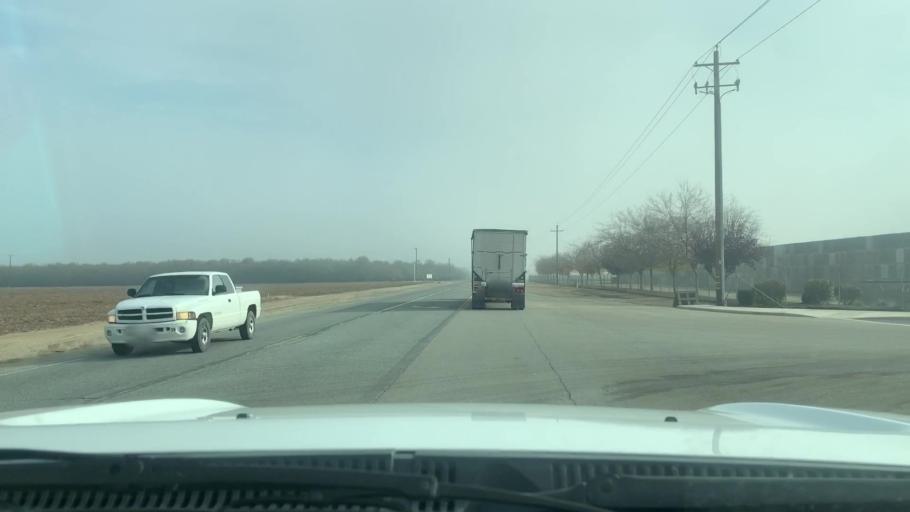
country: US
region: California
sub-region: Kern County
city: Buttonwillow
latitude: 35.5008
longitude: -119.5264
